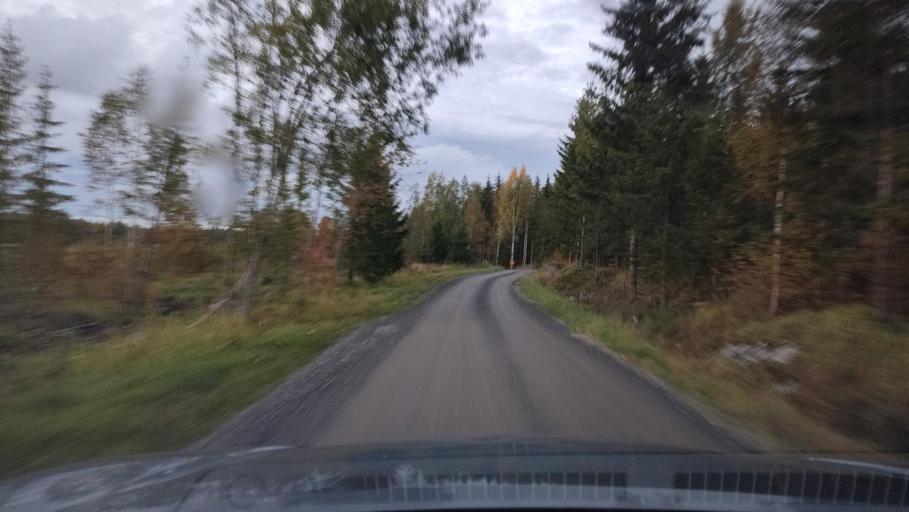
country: FI
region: Ostrobothnia
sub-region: Sydosterbotten
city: Kristinestad
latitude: 62.2795
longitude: 21.5150
